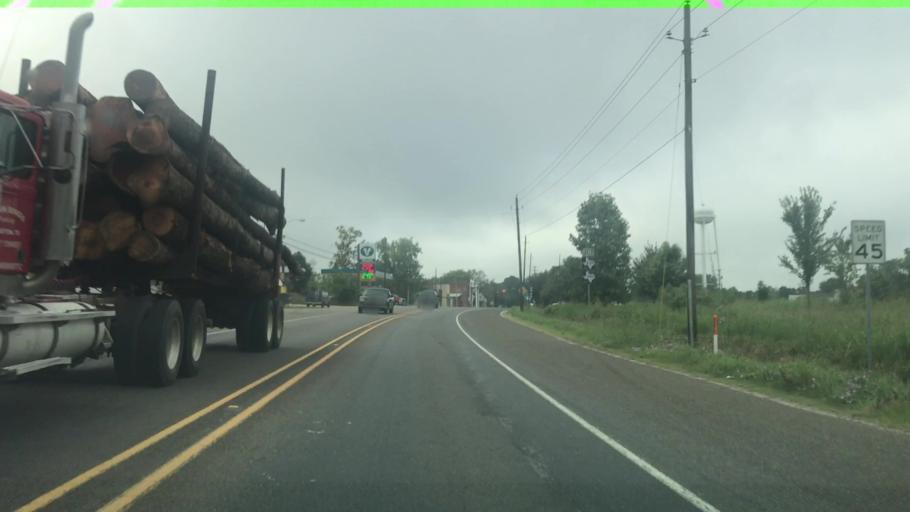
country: US
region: Texas
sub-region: Houston County
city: Cooper
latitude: 31.1294
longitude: -95.4460
